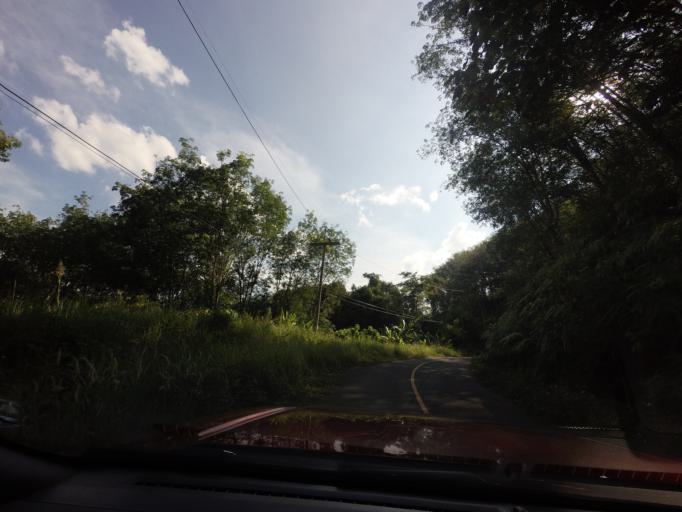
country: TH
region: Narathiwat
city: Si Sakhon
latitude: 6.0632
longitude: 101.3815
